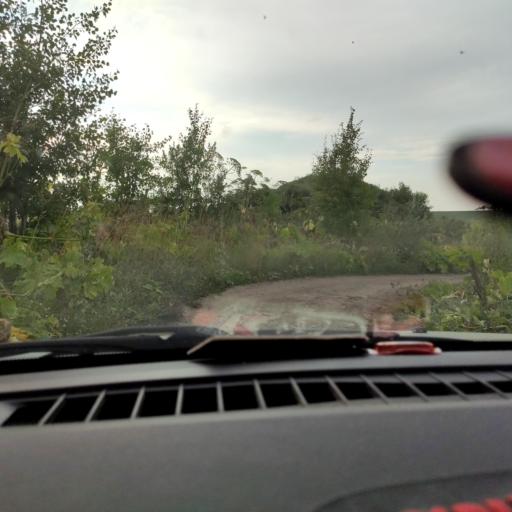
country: RU
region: Perm
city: Kultayevo
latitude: 57.8570
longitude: 55.9687
